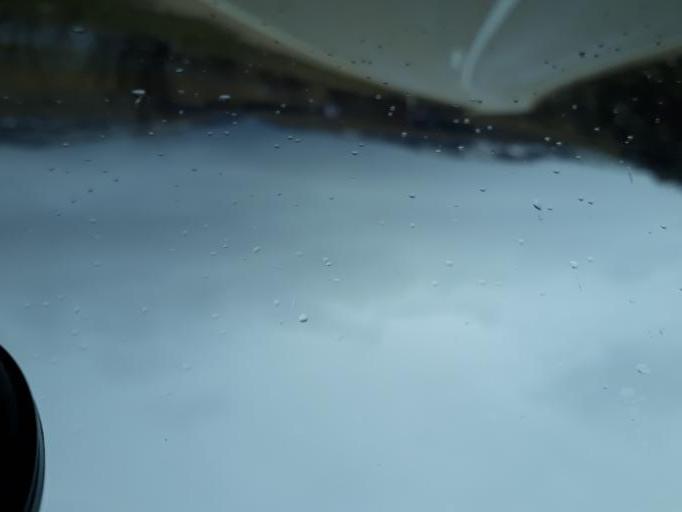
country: BA
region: Federation of Bosnia and Herzegovina
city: Tomislavgrad
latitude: 43.8323
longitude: 17.1880
